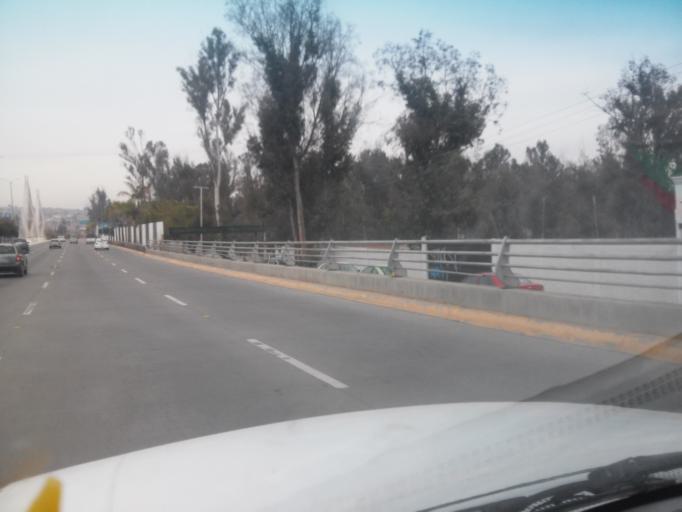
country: MX
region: Durango
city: Victoria de Durango
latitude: 24.0226
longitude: -104.6901
